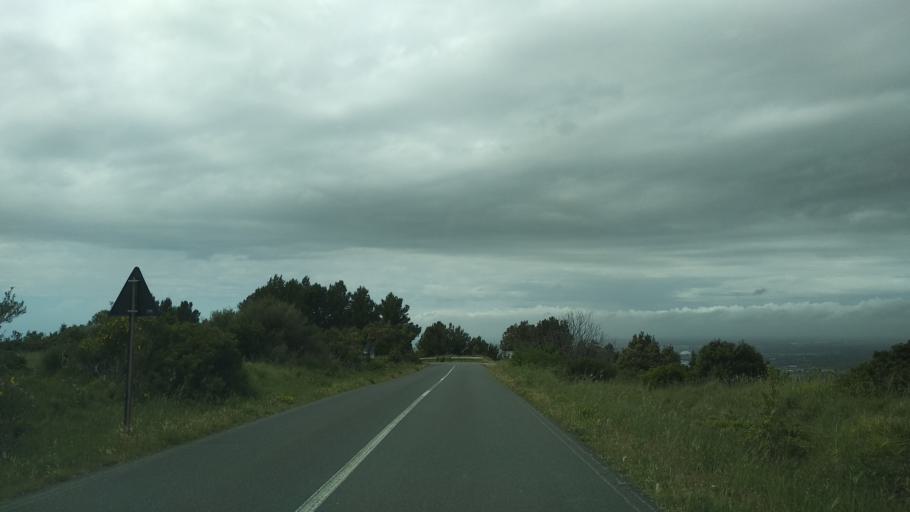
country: IT
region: Tuscany
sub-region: Provincia di Livorno
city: Quercianella
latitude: 43.4956
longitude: 10.3593
